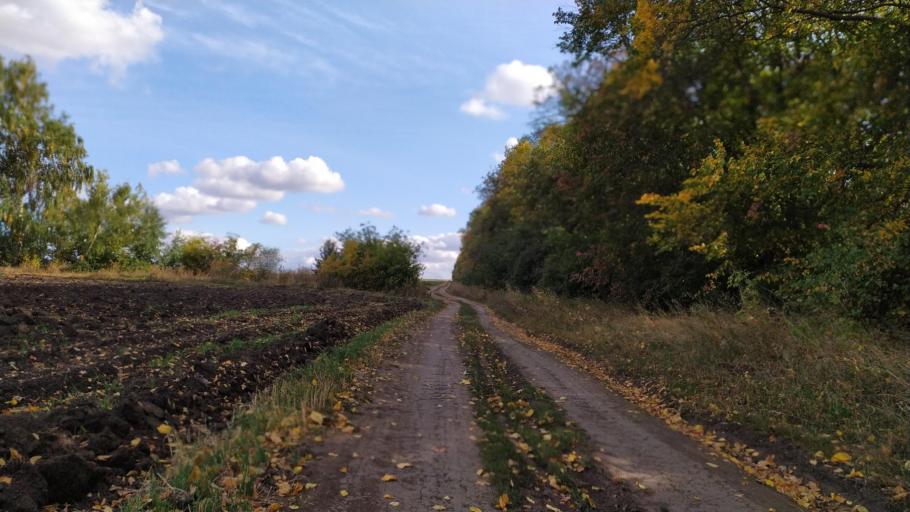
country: RU
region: Kursk
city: Kursk
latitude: 51.6225
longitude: 36.1613
